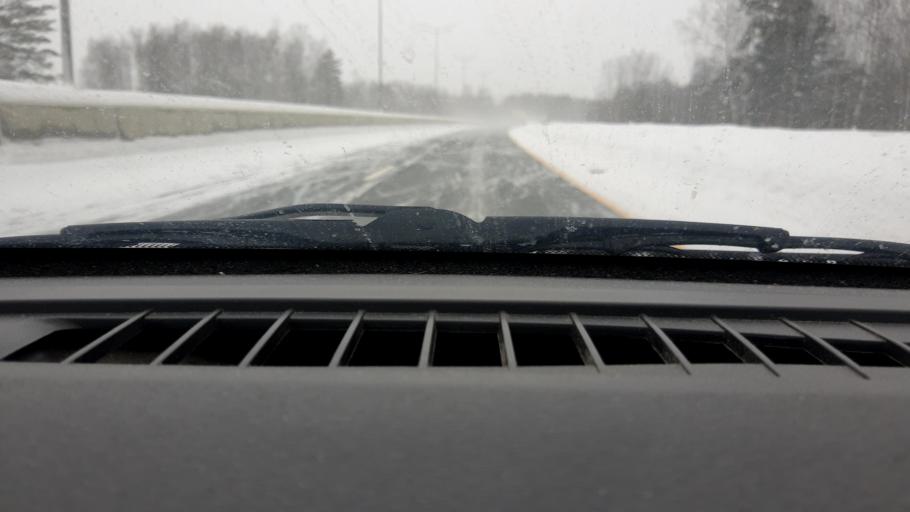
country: RU
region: Moskovskaya
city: Noginsk
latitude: 55.9213
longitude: 38.4810
